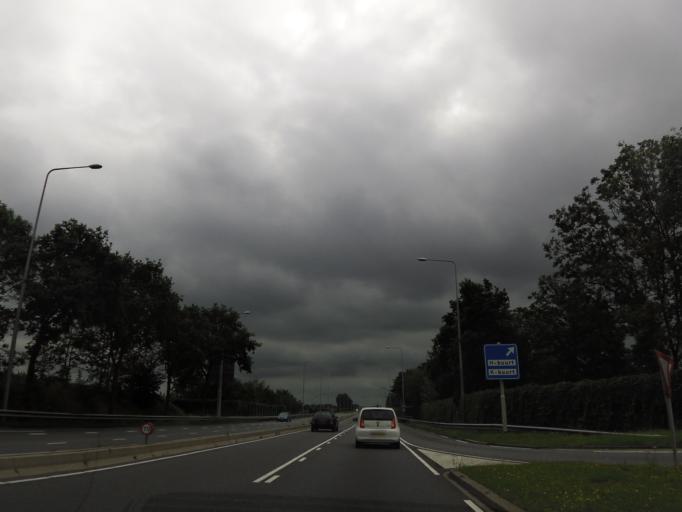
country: NL
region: North Holland
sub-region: Gemeente Amsterdam
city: Amsterdam-Zuidoost
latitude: 52.3155
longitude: 4.9645
